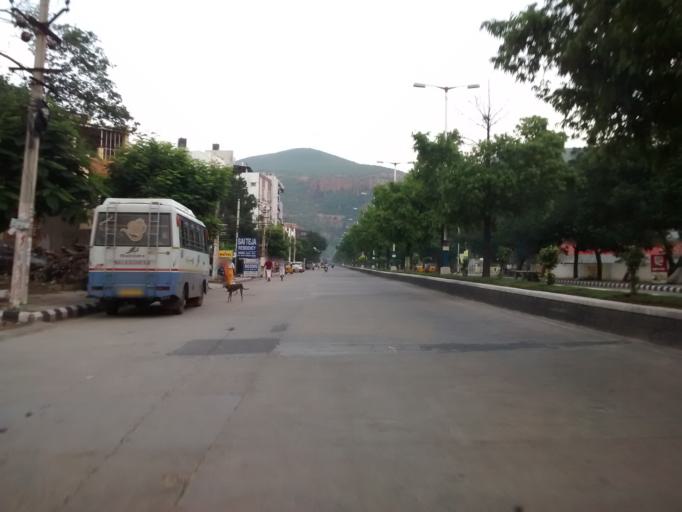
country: IN
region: Andhra Pradesh
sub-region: Chittoor
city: Akkarampalle
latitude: 13.6484
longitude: 79.4254
